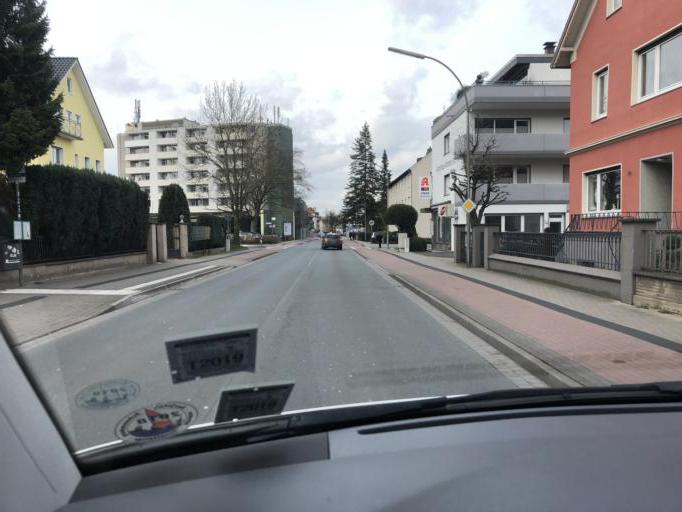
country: DE
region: North Rhine-Westphalia
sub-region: Regierungsbezirk Detmold
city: Herford
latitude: 52.1094
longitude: 8.6746
